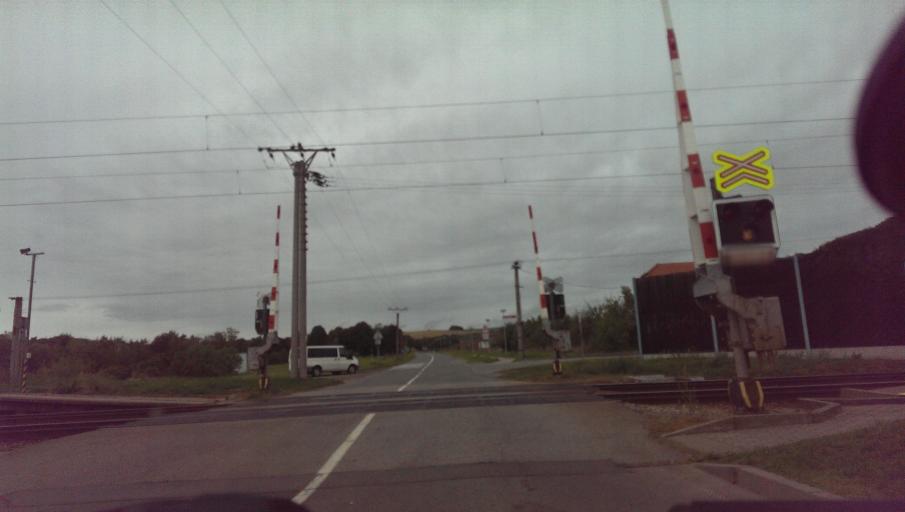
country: CZ
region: South Moravian
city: Moravsky Pisek
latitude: 48.9908
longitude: 17.3299
